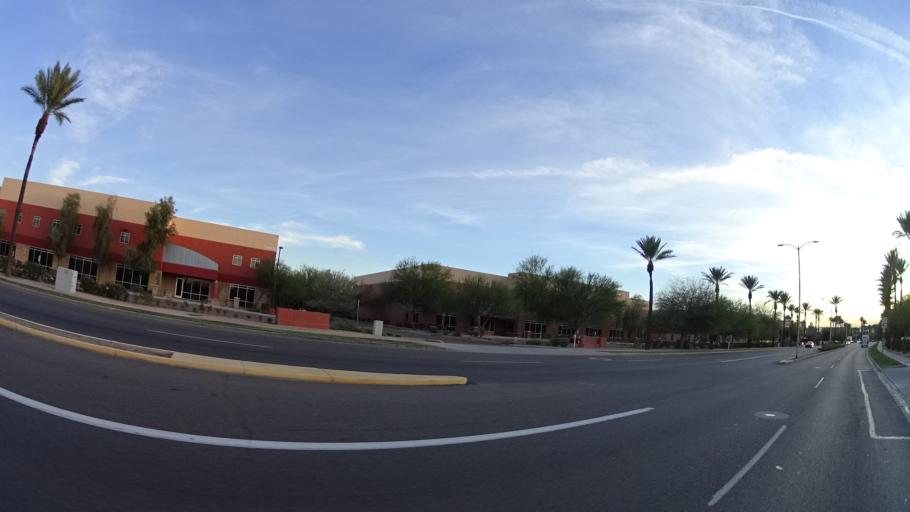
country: US
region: Arizona
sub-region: Maricopa County
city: Tempe Junction
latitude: 33.4184
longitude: -112.0053
